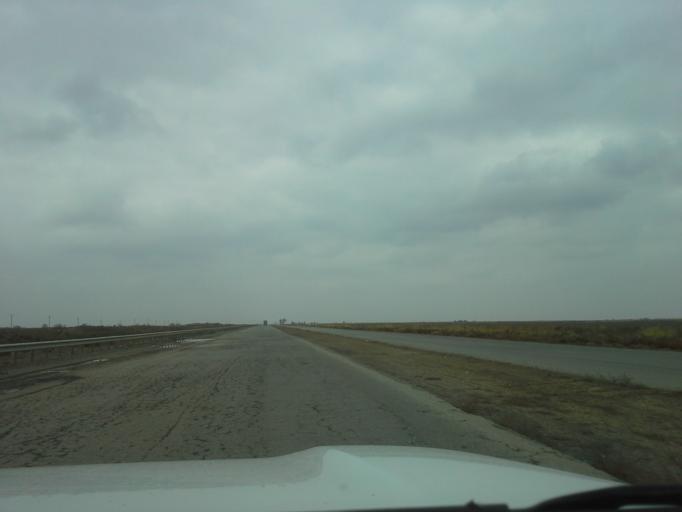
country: TM
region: Ahal
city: Tejen
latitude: 37.2870
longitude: 60.8004
